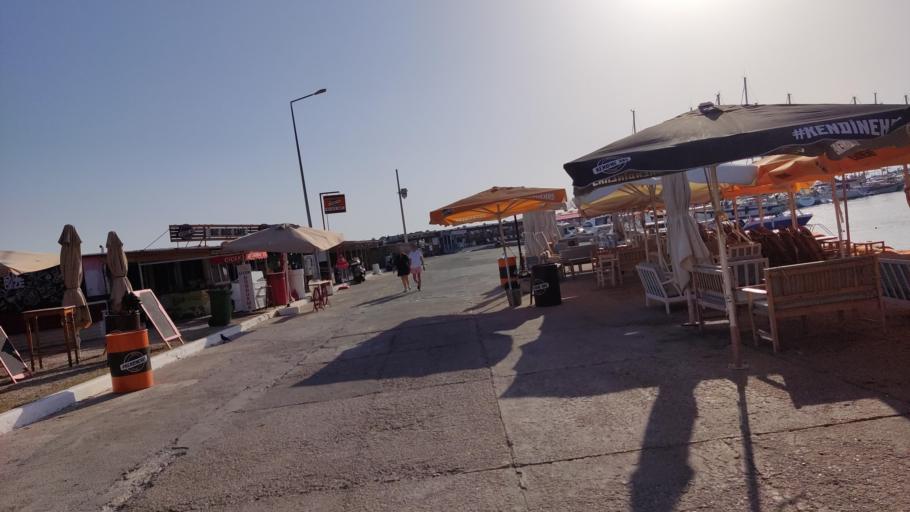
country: TR
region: Canakkale
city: Bozcaada
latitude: 39.8359
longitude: 26.0735
